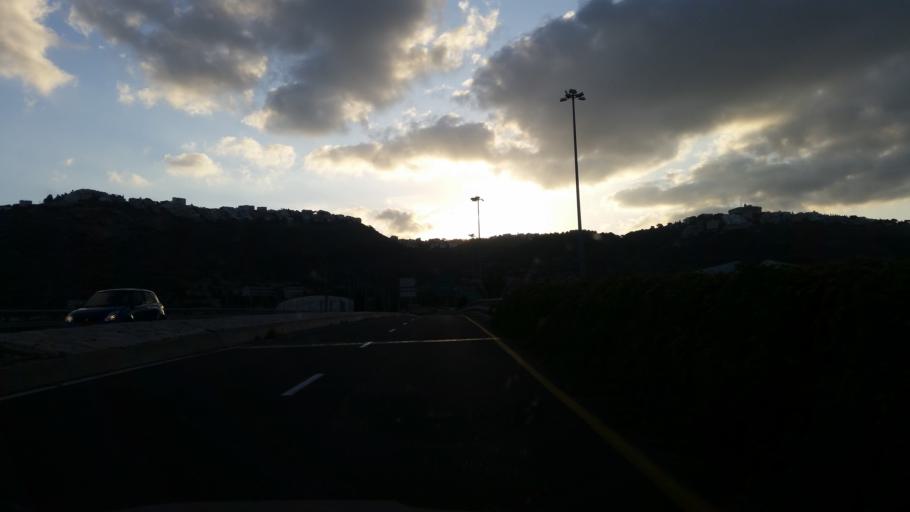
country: IL
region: Haifa
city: Tirat Karmel
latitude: 32.7926
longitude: 34.9613
